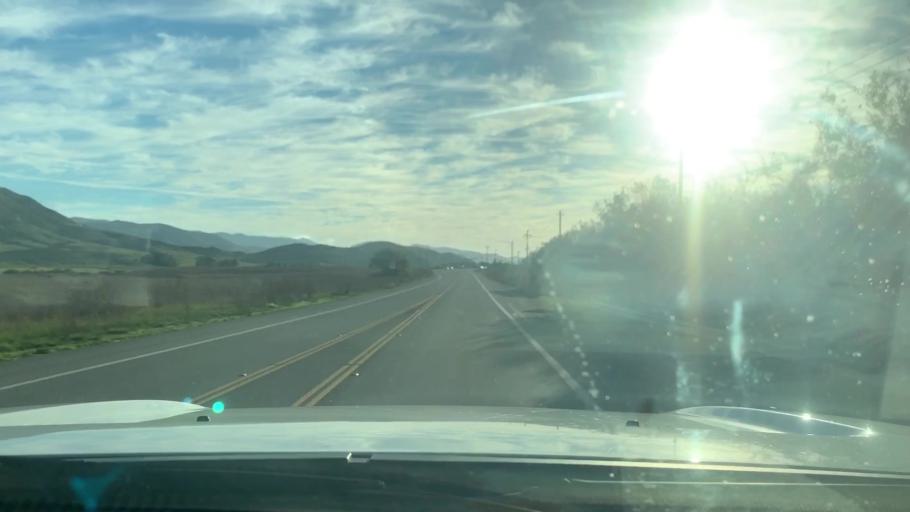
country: US
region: California
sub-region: San Luis Obispo County
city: San Luis Obispo
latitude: 35.2786
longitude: -120.7167
